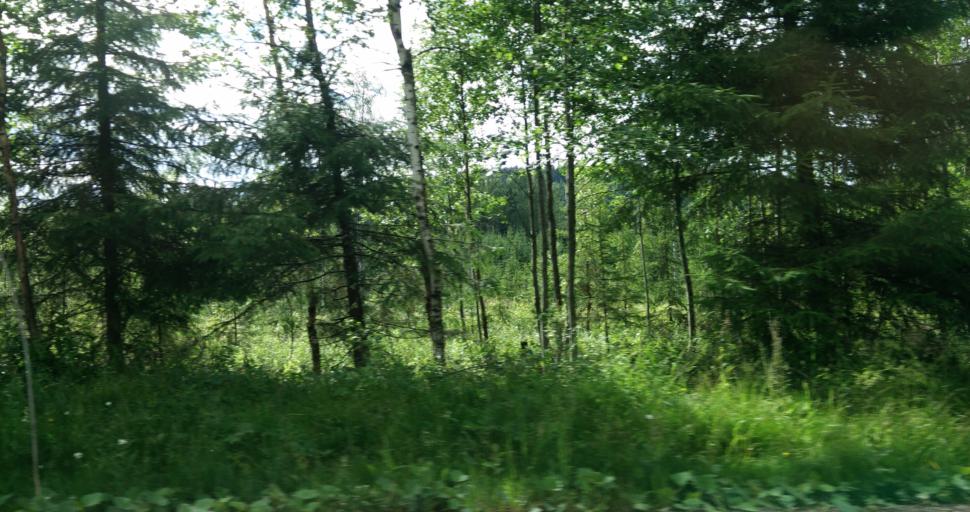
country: SE
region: Vaermland
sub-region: Hagfors Kommun
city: Ekshaerad
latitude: 60.0222
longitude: 13.4817
